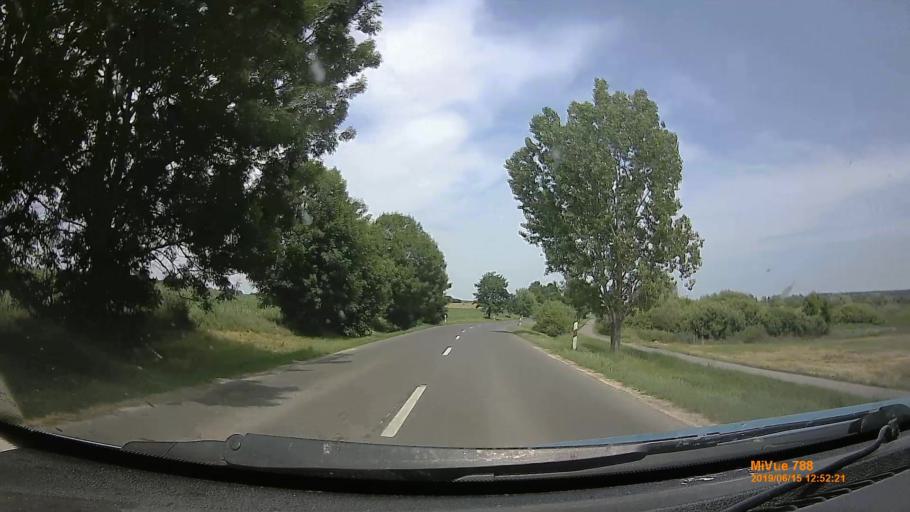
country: HU
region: Baranya
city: Sasd
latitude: 46.2960
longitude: 18.1231
